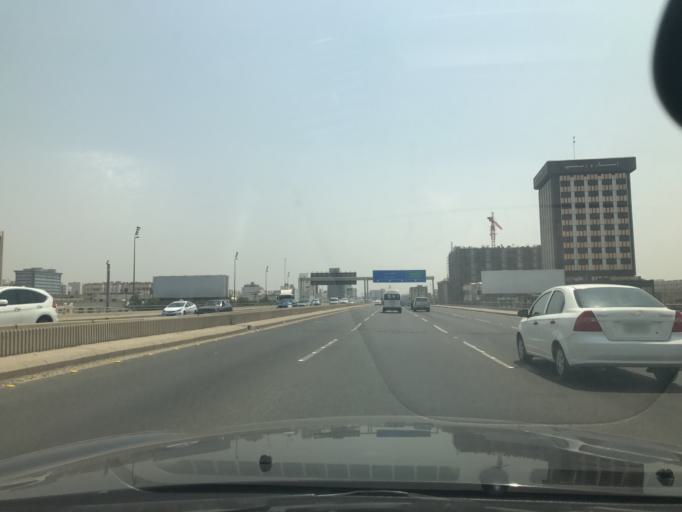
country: SA
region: Makkah
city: Jeddah
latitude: 21.4768
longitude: 39.1803
